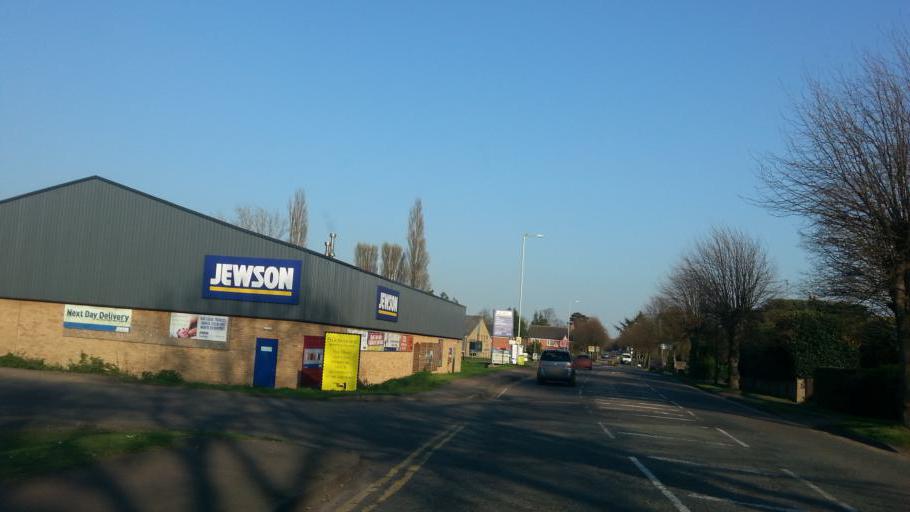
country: GB
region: England
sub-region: Northamptonshire
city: Rushden
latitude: 52.2961
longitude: -0.6219
